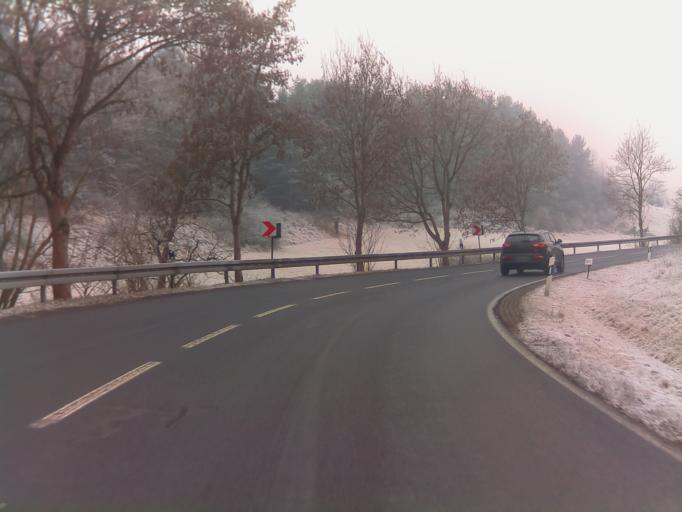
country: DE
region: Thuringia
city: Rohr
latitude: 50.6050
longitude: 10.5081
